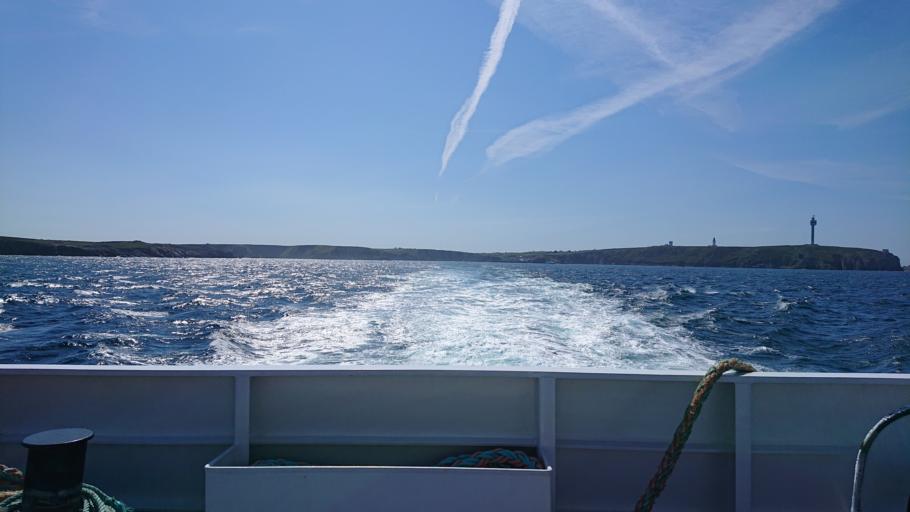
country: FR
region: Brittany
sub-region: Departement du Finistere
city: Porspoder
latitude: 48.4704
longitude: -5.0302
